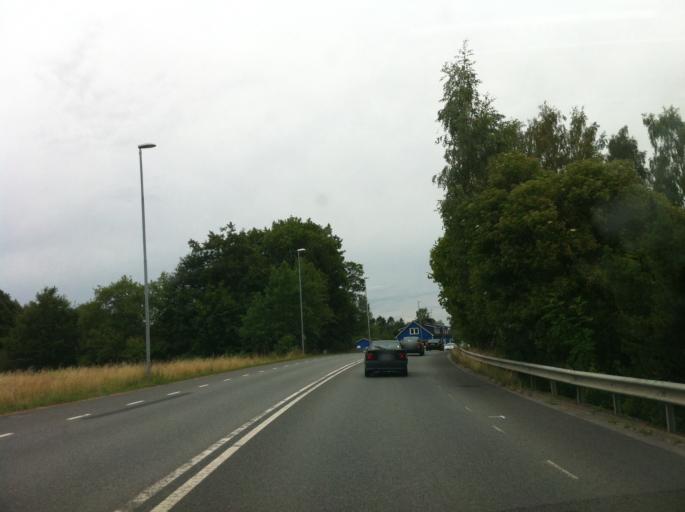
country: SE
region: Skane
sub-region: Hoors Kommun
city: Hoeoer
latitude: 55.9470
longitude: 13.5599
